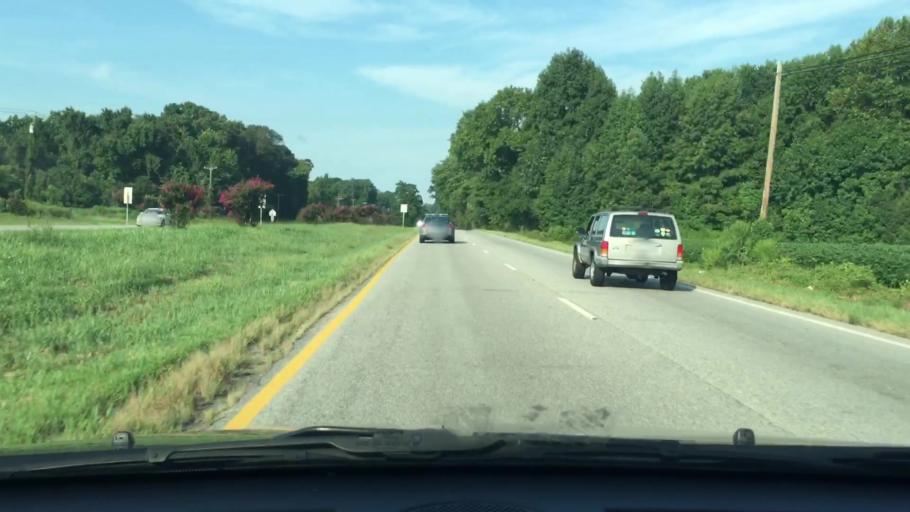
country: US
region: Virginia
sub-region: Isle of Wight County
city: Carrollton
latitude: 36.9428
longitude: -76.5581
